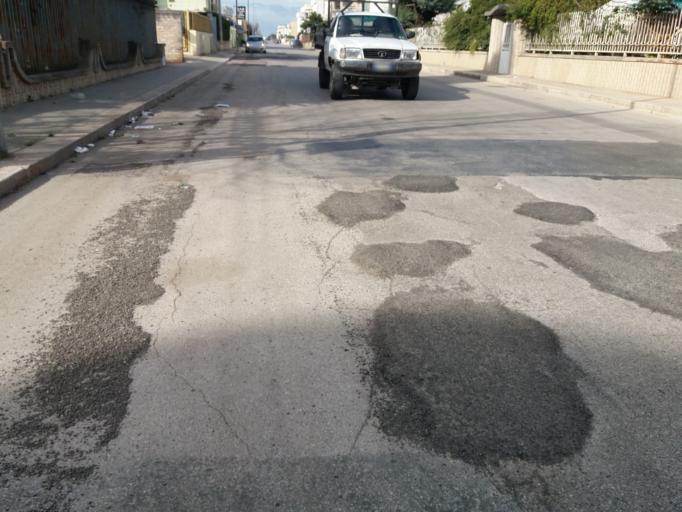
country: IT
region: Apulia
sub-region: Provincia di Bari
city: Bitonto
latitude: 41.1105
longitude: 16.6781
